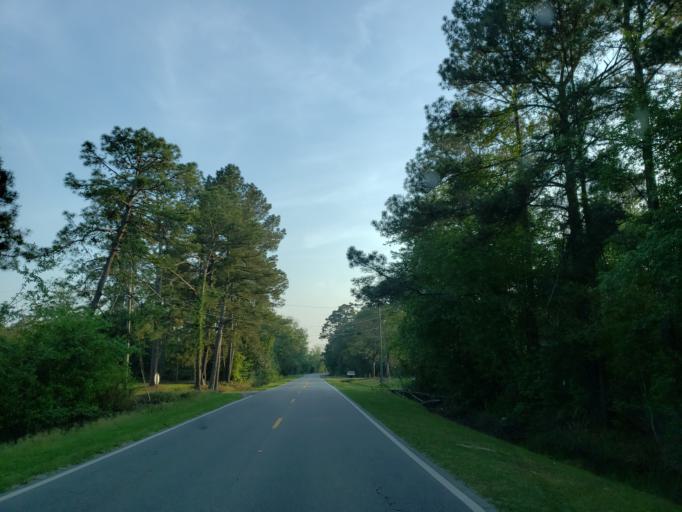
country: US
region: Georgia
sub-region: Cook County
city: Sparks
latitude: 31.1704
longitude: -83.4332
